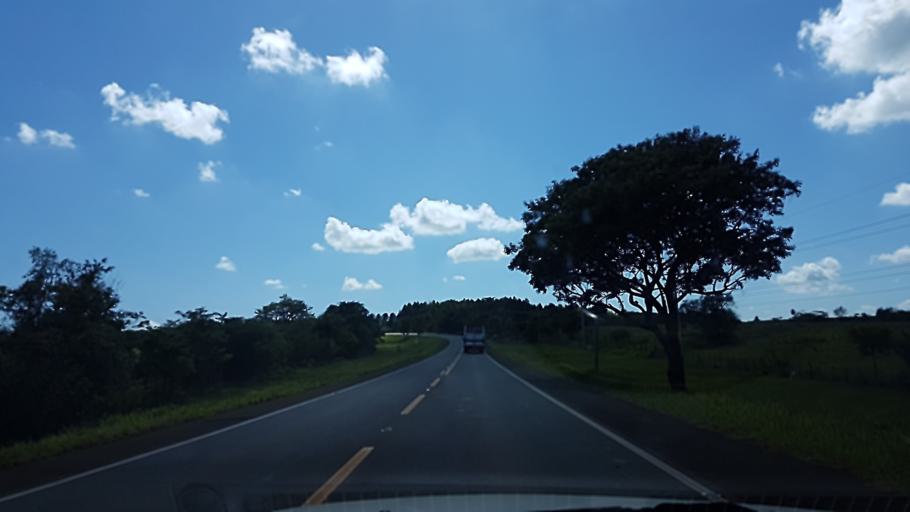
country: PY
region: Itapua
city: Carmen del Parana
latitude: -27.2206
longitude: -56.1035
